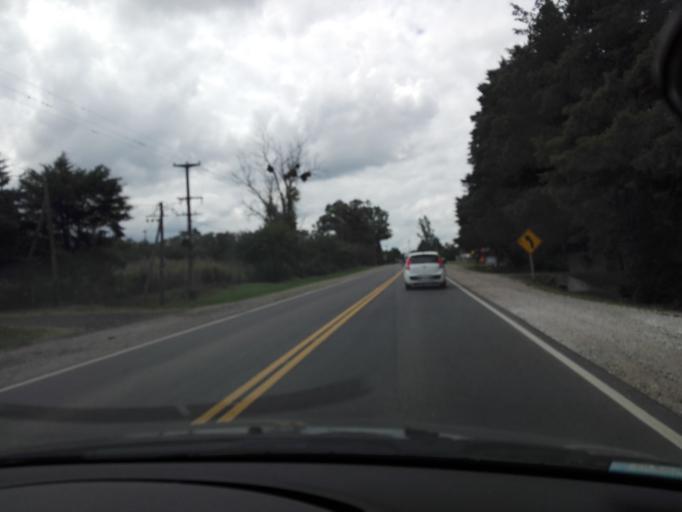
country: AR
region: Cordoba
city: Alta Gracia
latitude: -31.5967
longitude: -64.4531
